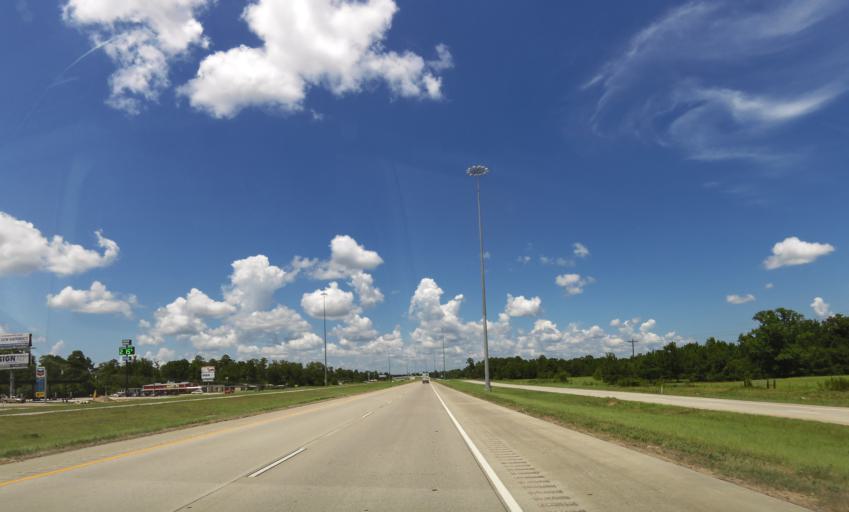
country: US
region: Texas
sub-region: San Jacinto County
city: Shepherd
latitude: 30.4879
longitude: -94.9946
